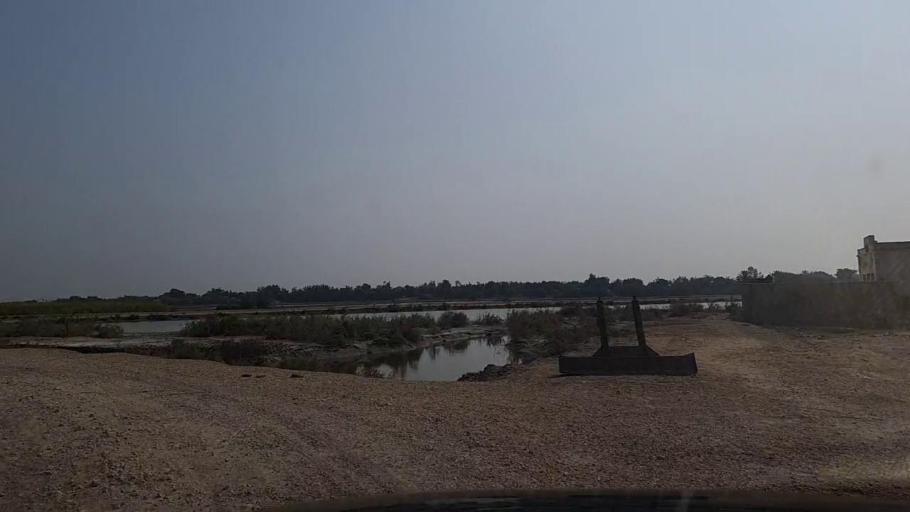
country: PK
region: Sindh
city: Mirpur Batoro
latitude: 24.6851
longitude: 68.2224
